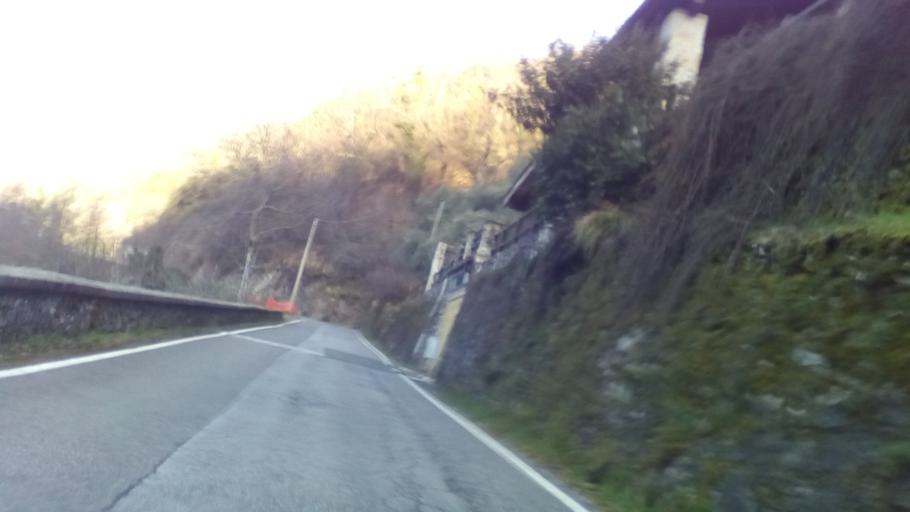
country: IT
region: Tuscany
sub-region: Provincia di Massa-Carrara
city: Montignoso
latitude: 44.0528
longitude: 10.1912
